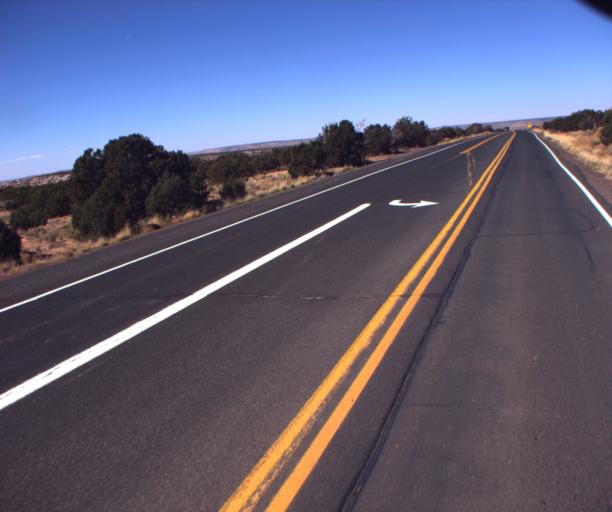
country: US
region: Arizona
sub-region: Navajo County
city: First Mesa
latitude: 35.8449
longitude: -110.5310
